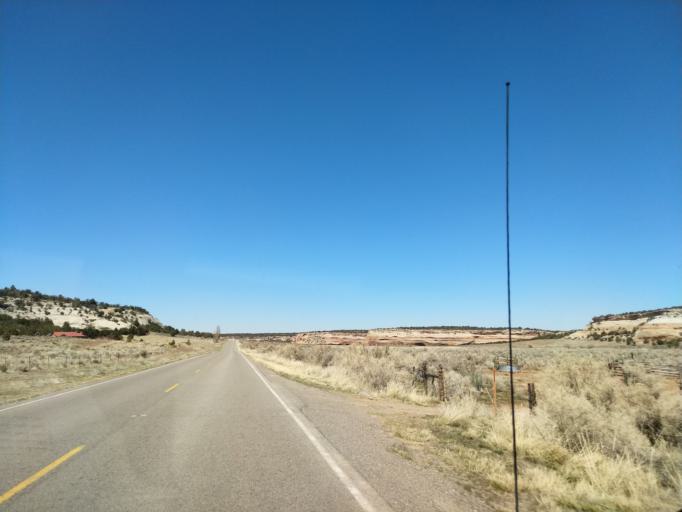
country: US
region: Colorado
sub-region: Mesa County
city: Fruita
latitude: 38.9977
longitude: -108.8290
